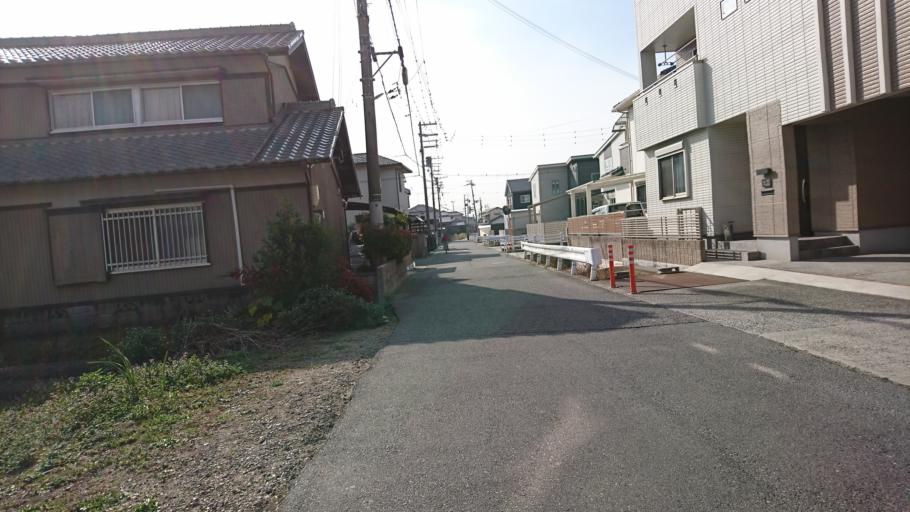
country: JP
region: Hyogo
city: Kakogawacho-honmachi
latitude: 34.7462
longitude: 134.8448
